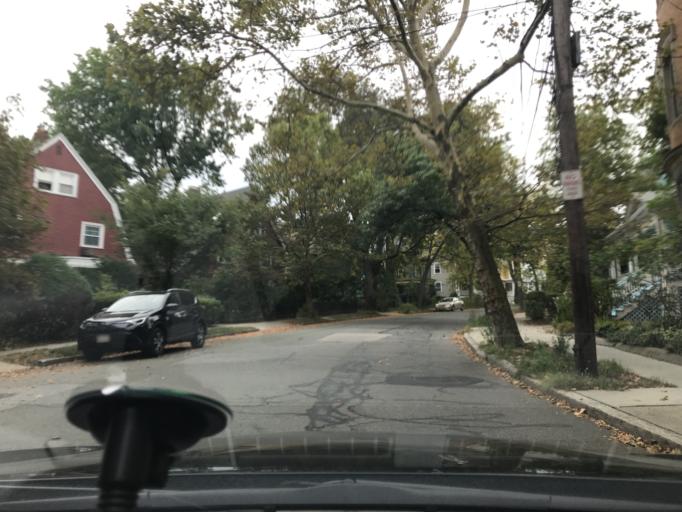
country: US
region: Massachusetts
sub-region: Norfolk County
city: Brookline
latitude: 42.3480
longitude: -71.1242
